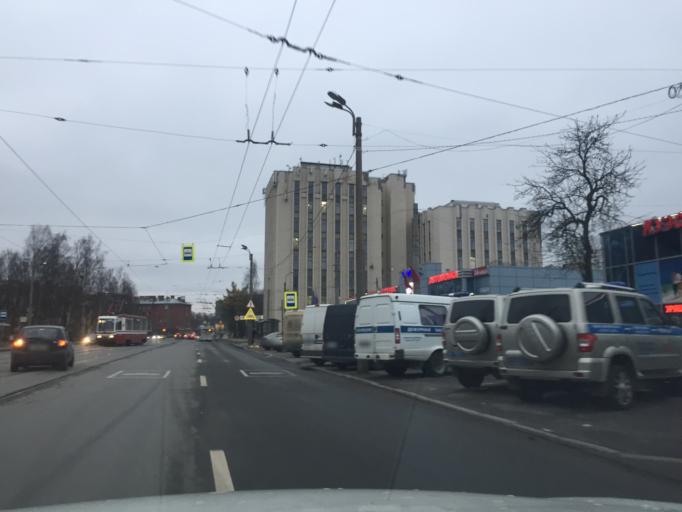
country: RU
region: St.-Petersburg
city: Kushelevka
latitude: 60.0116
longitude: 30.3689
